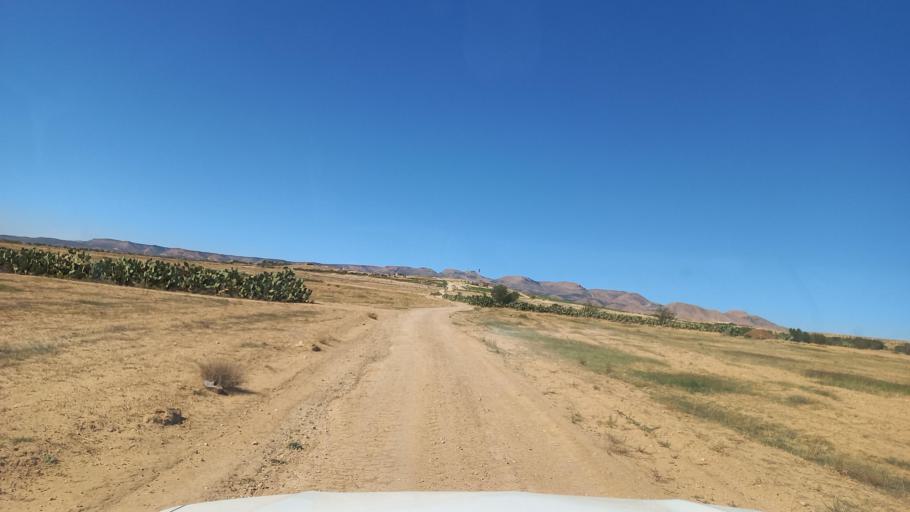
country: TN
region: Al Qasrayn
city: Sbiba
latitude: 35.3710
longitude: 9.0837
